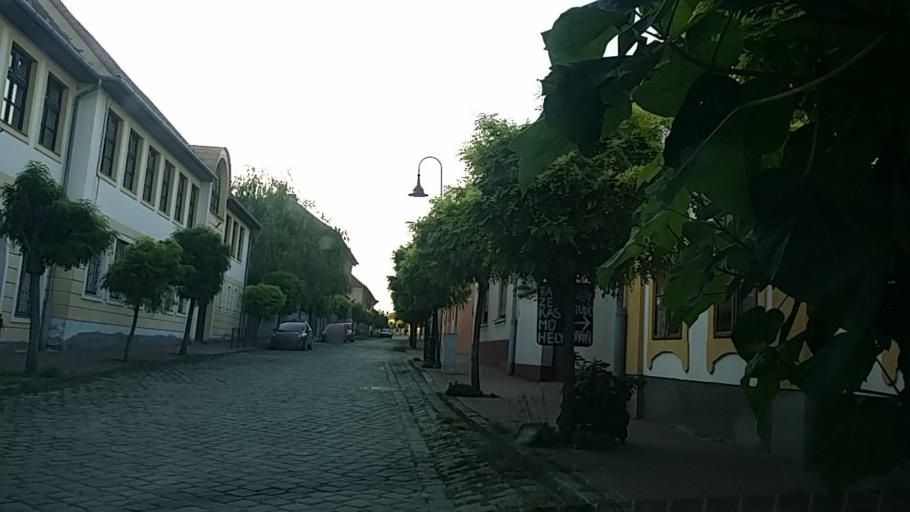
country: HU
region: Tolna
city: Dunafoldvar
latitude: 46.8080
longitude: 18.9270
